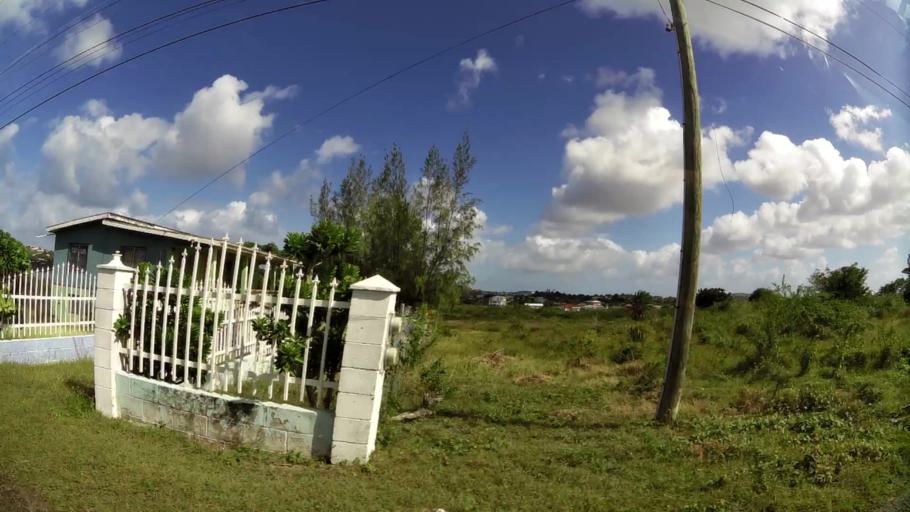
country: AG
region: Saint John
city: Saint John's
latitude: 17.1390
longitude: -61.8569
